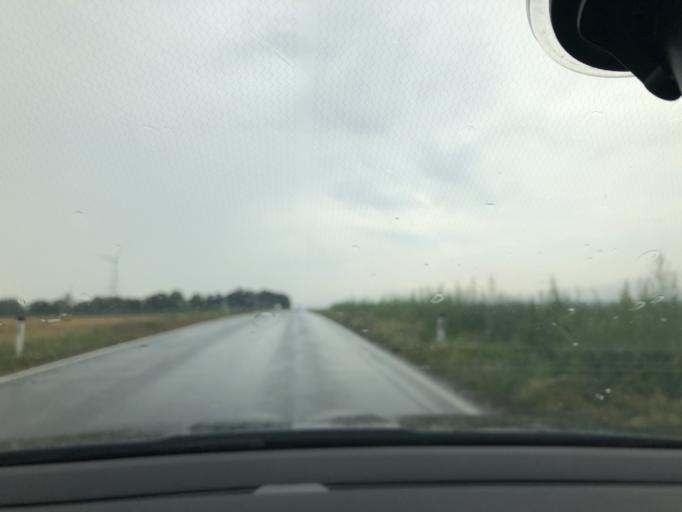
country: AT
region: Lower Austria
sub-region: Politischer Bezirk Ganserndorf
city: Auersthal
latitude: 48.3594
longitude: 16.6691
